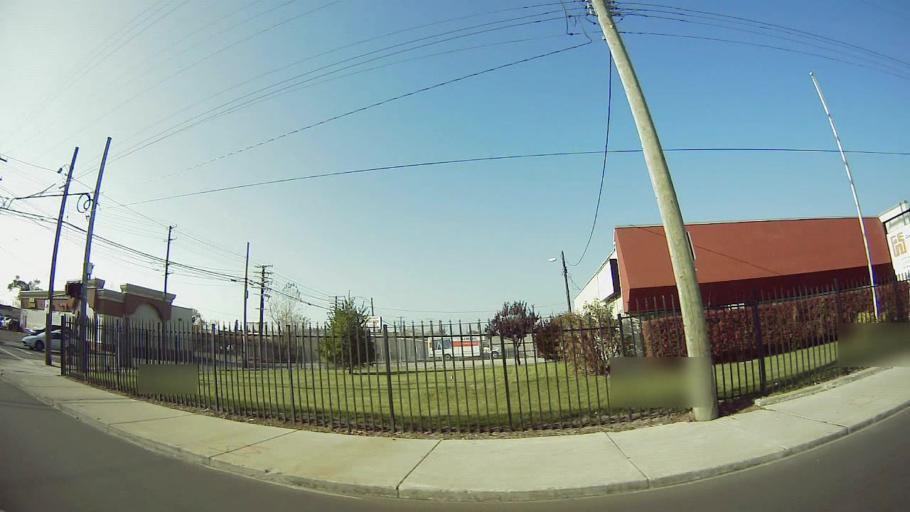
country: US
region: Michigan
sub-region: Oakland County
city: Oak Park
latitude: 42.3950
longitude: -83.1788
